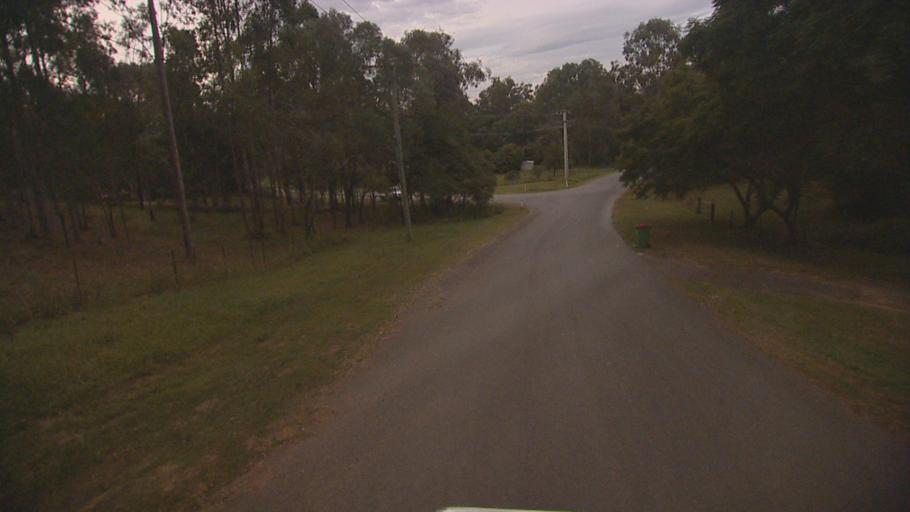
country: AU
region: Queensland
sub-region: Logan
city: Chambers Flat
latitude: -27.8209
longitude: 153.0913
